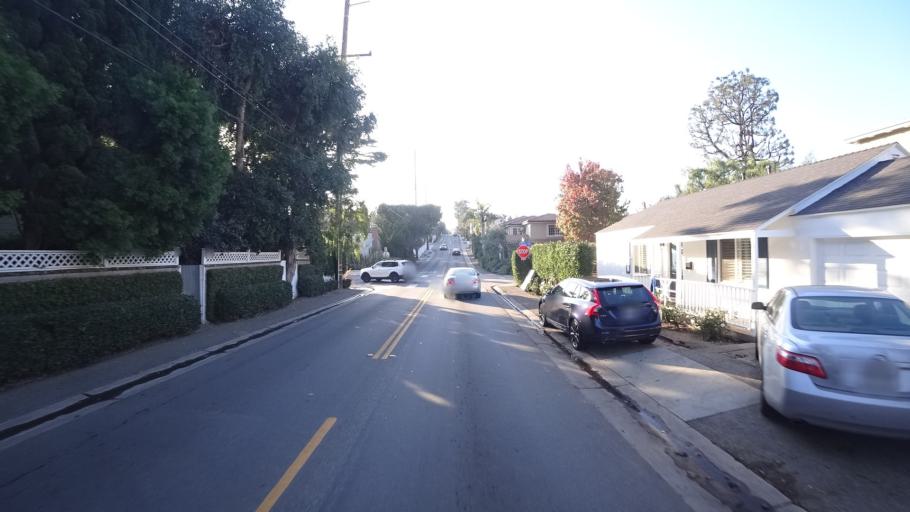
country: US
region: California
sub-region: Los Angeles County
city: Manhattan Beach
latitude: 33.8946
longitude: -118.3992
